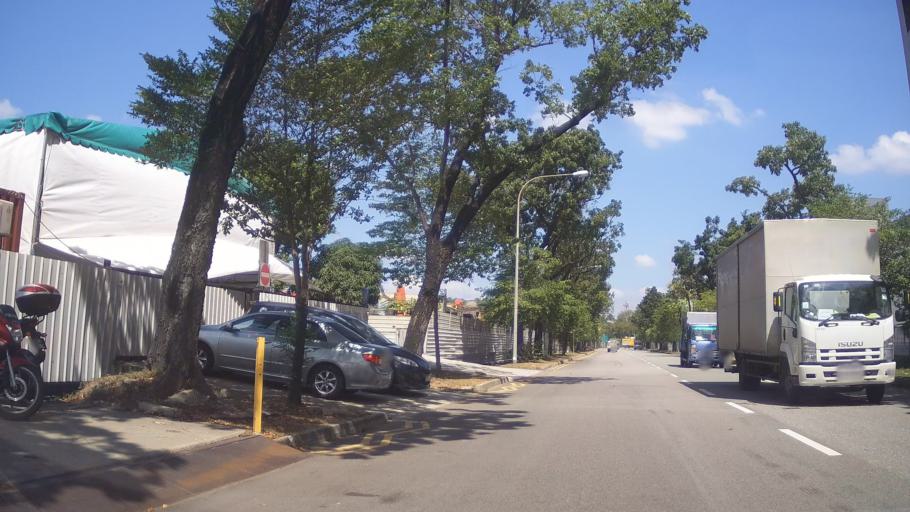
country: SG
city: Singapore
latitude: 1.3115
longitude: 103.6930
